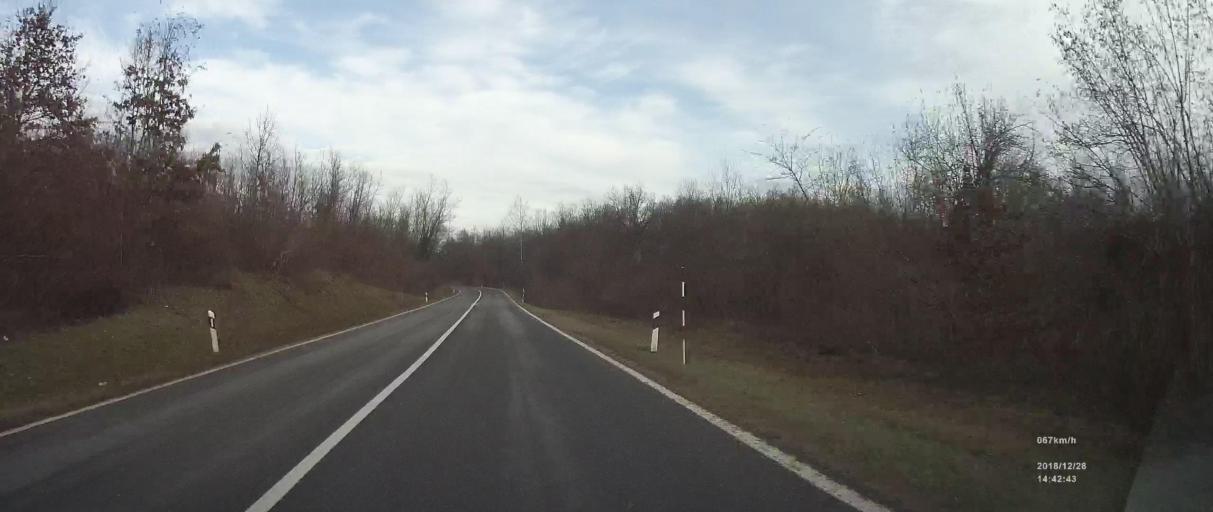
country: SI
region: Crnomelj
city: Crnomelj
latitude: 45.4440
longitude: 15.2699
